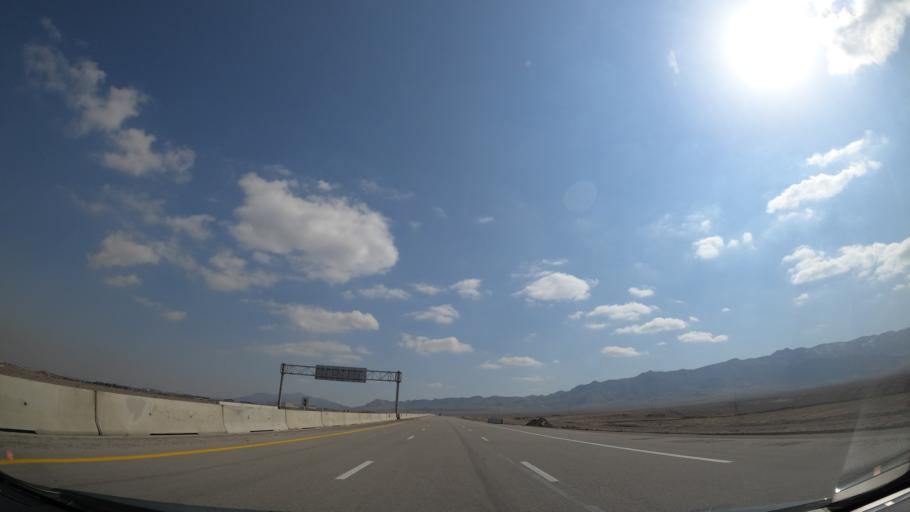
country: IR
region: Alborz
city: Eshtehard
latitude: 35.7252
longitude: 50.5645
